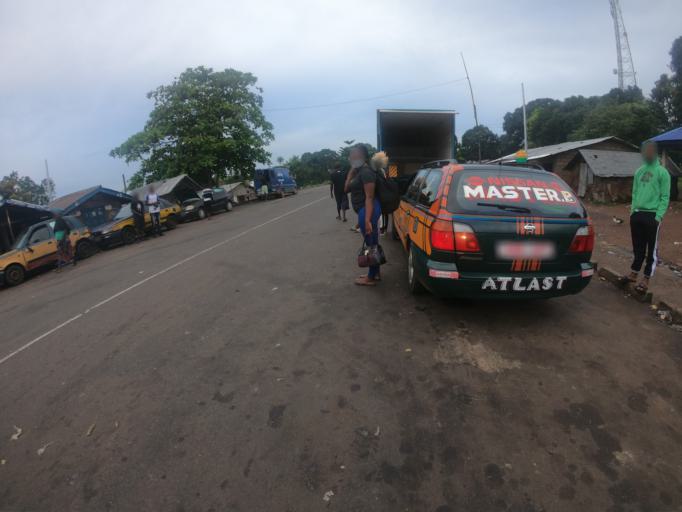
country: SL
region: Northern Province
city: Port Loko
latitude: 8.4910
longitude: -12.7581
